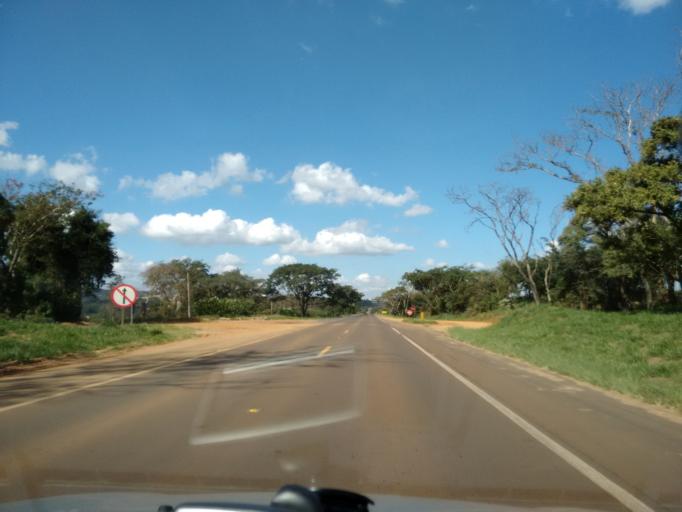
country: BR
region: Sao Paulo
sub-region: Sao Carlos
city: Sao Carlos
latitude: -22.0647
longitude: -47.9284
